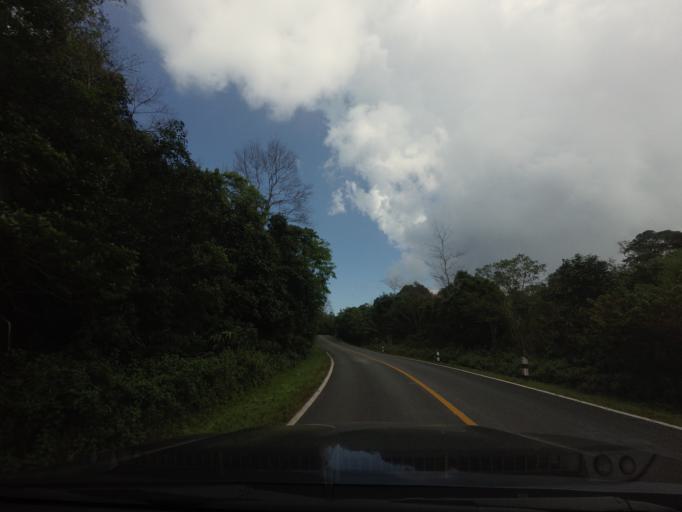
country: TH
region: Phetchabun
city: Lom Kao
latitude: 16.9590
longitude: 101.0219
